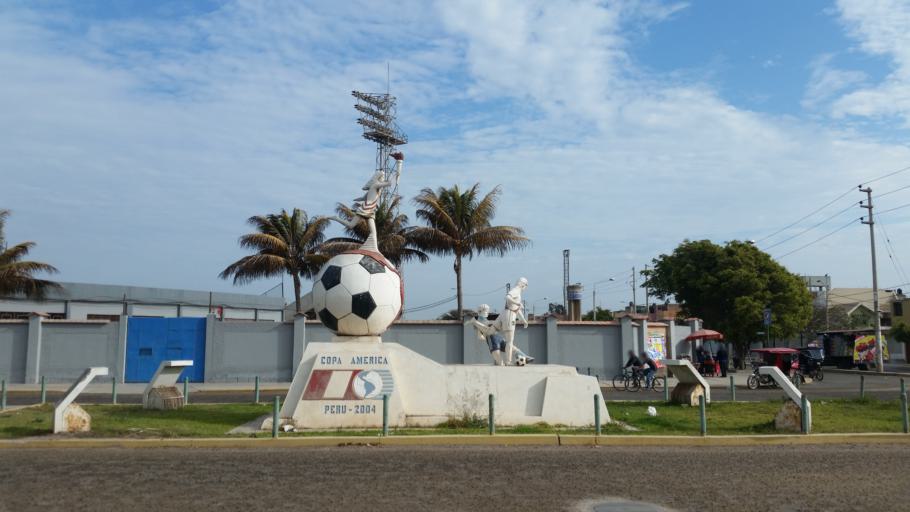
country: PE
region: Lambayeque
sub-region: Provincia de Chiclayo
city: Chiclayo
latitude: -6.7697
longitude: -79.8604
